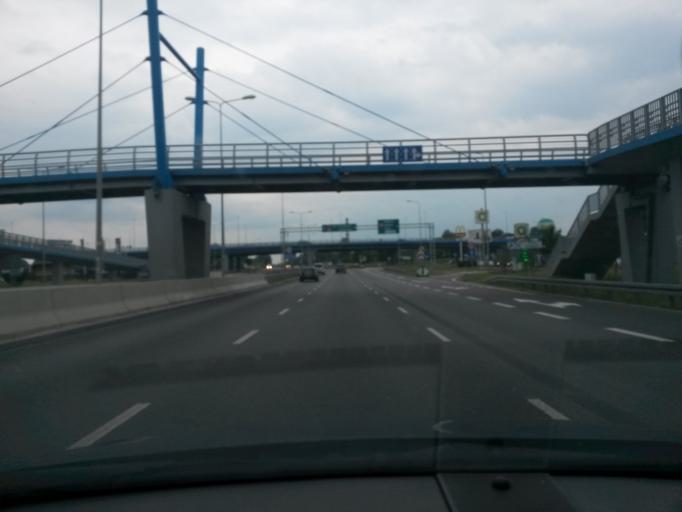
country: PL
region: Silesian Voivodeship
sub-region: Czestochowa
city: Czestochowa
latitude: 50.8197
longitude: 19.1393
